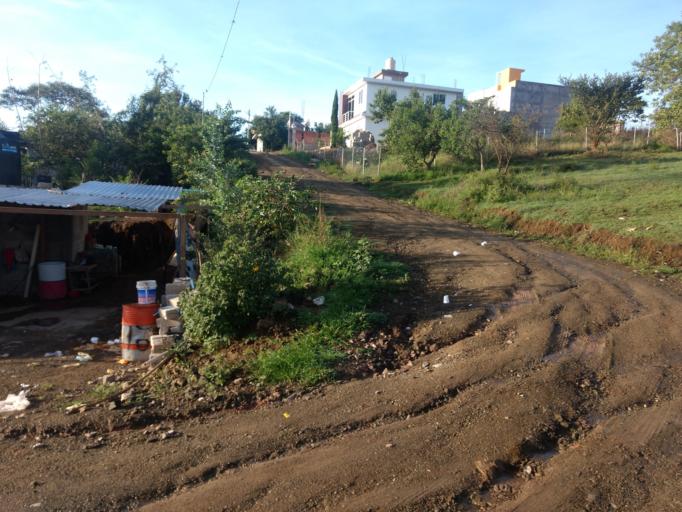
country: MX
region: Oaxaca
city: Ciudad de Huajuapam de Leon
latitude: 17.8309
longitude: -97.7857
